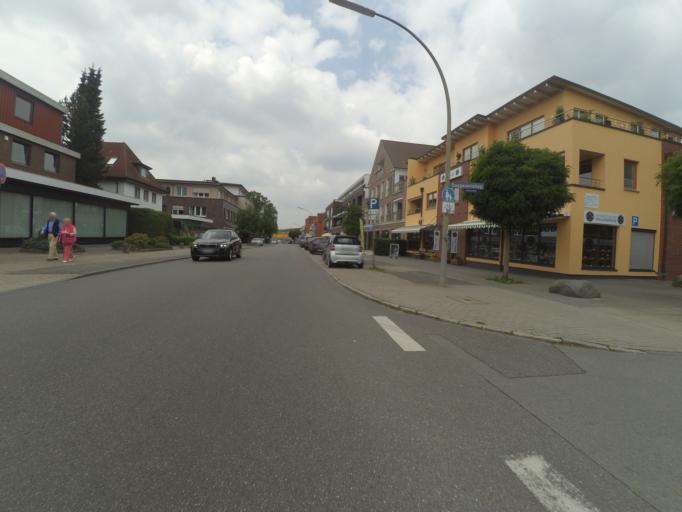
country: DE
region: Hamburg
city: Poppenbuettel
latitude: 53.6512
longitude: 10.0968
